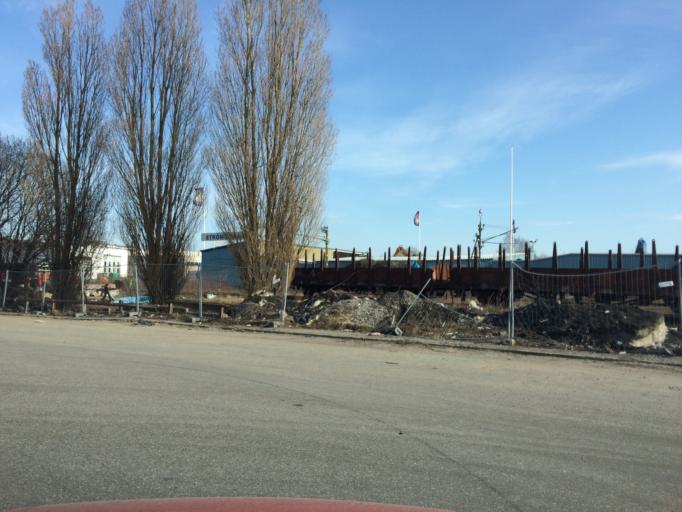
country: SE
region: Stockholm
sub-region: Stockholms Kommun
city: Arsta
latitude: 59.2983
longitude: 18.0199
